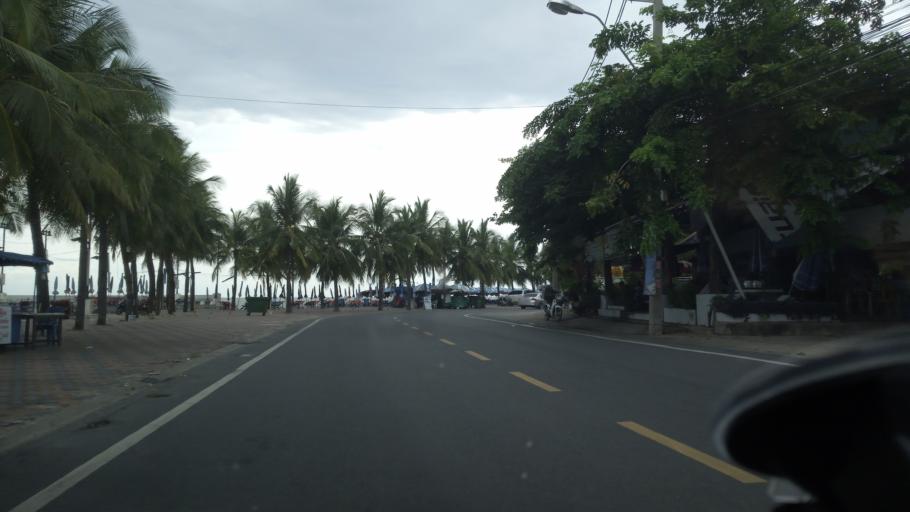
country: TH
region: Chon Buri
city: Chon Buri
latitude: 13.3002
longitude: 100.8997
